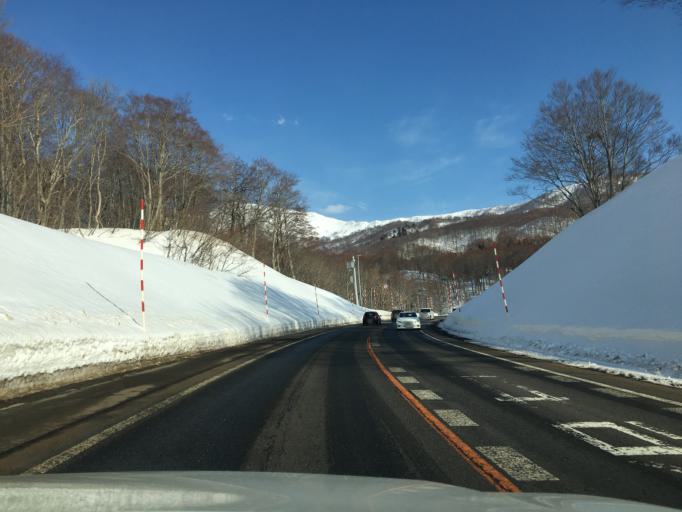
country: JP
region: Yamagata
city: Tsuruoka
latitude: 38.5331
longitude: 139.9477
